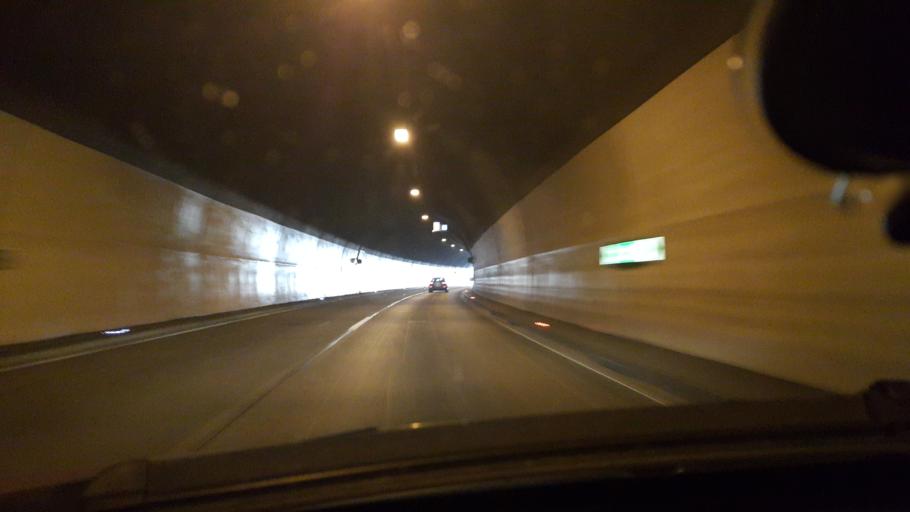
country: SI
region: Slovenska Konjice
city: Slovenske Konjice
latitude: 46.3122
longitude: 15.4565
